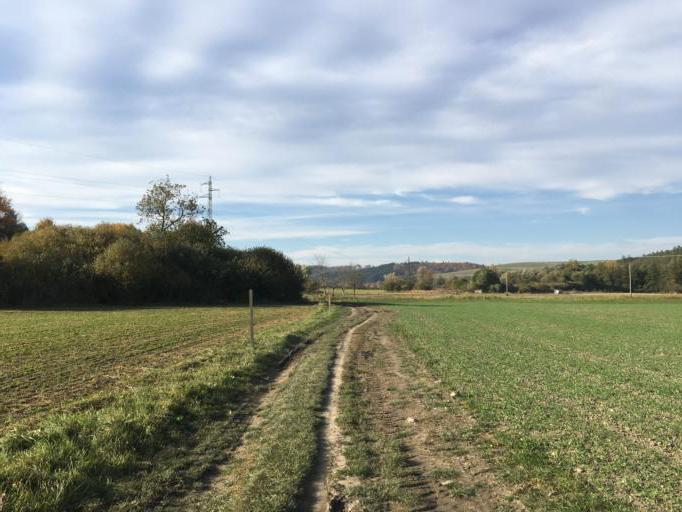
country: SK
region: Trenciansky
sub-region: Okres Povazska Bystrica
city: Povazska Bystrica
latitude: 49.0419
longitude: 18.4285
